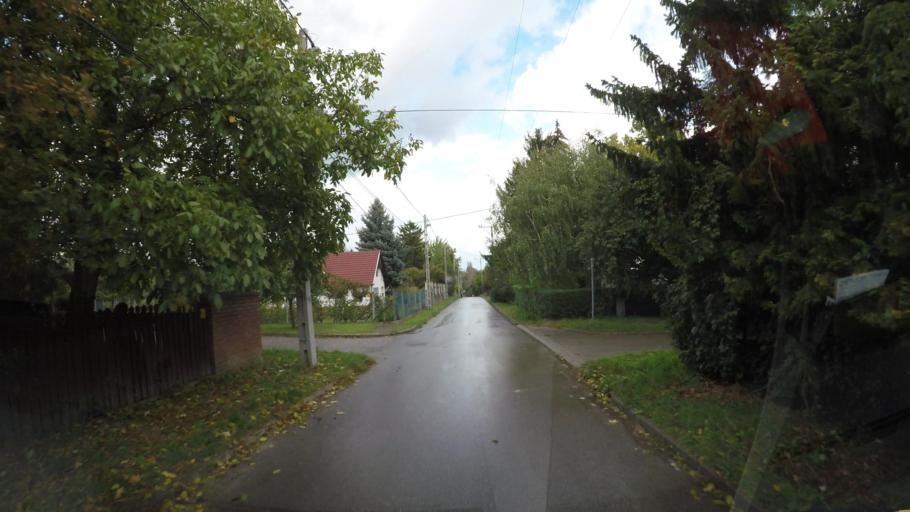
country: HU
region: Pest
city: Tahitotfalu
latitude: 47.7491
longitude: 19.0772
